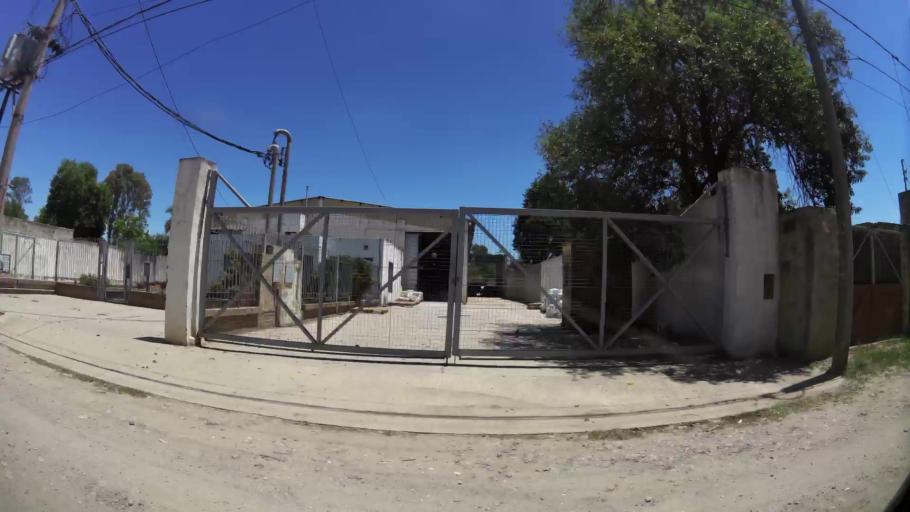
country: AR
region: Cordoba
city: Malvinas Argentinas
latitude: -31.3817
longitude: -64.1282
